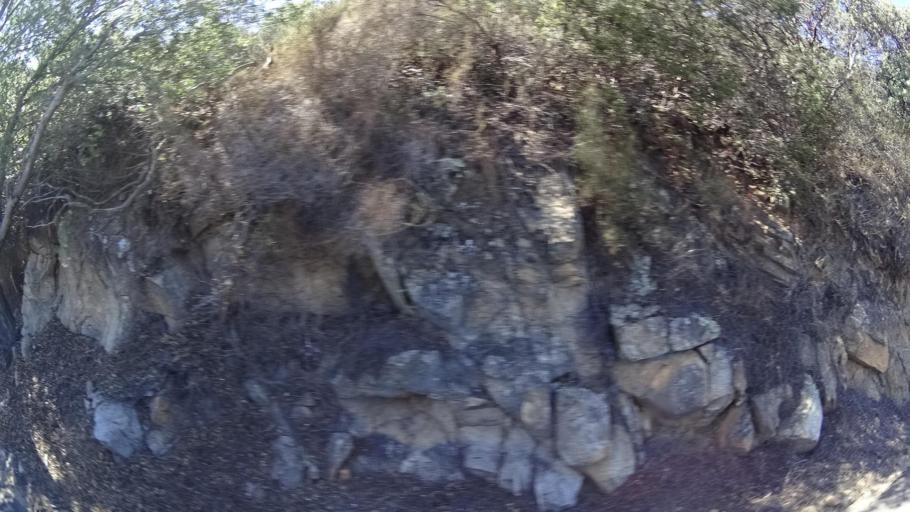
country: US
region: California
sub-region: San Diego County
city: Alpine
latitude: 32.7740
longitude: -116.7079
